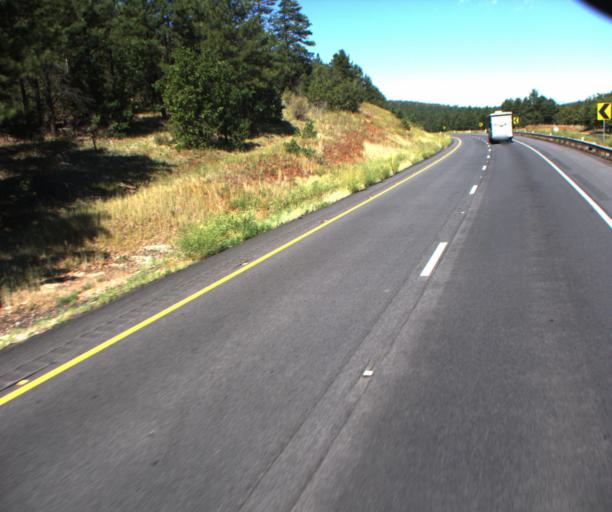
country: US
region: Arizona
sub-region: Coconino County
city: Williams
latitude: 35.2214
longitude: -112.2907
